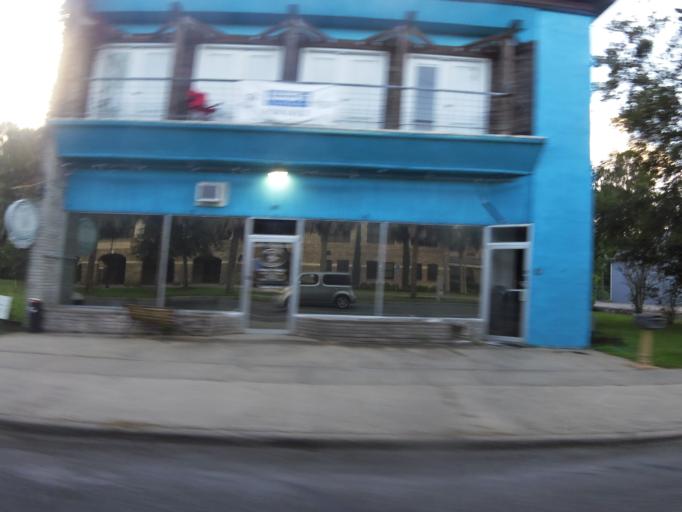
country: US
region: Georgia
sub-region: Camden County
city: St. Marys
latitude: 30.7283
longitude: -81.5468
